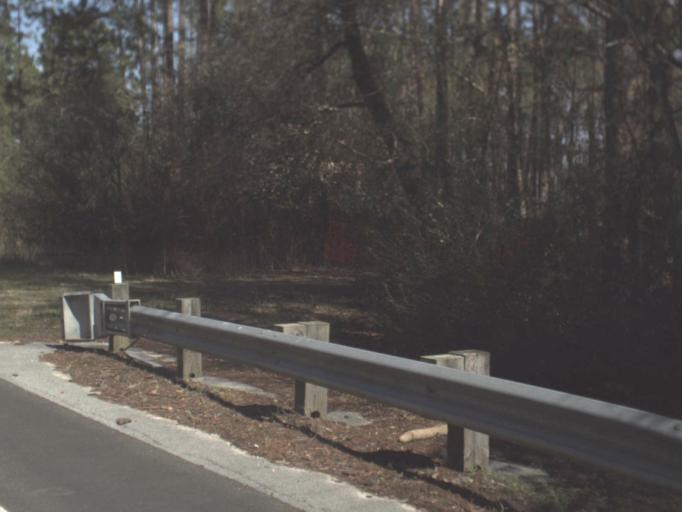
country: US
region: Florida
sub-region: Gulf County
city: Wewahitchka
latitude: 30.2470
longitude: -85.2057
